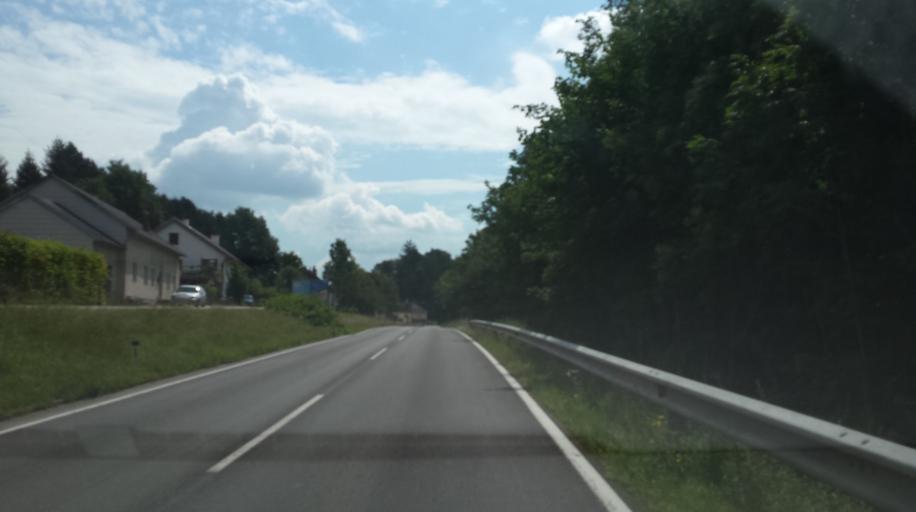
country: AT
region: Lower Austria
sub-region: Politischer Bezirk Amstetten
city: Haag
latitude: 48.1036
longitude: 14.5559
